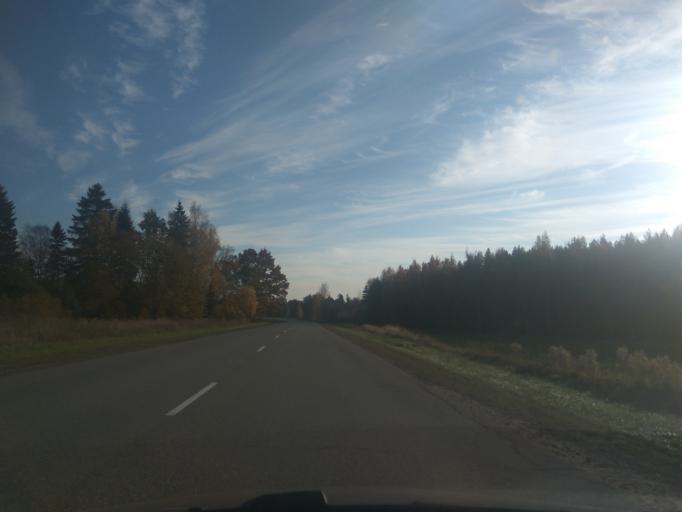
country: LV
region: Ventspils
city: Ventspils
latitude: 57.2908
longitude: 21.5650
